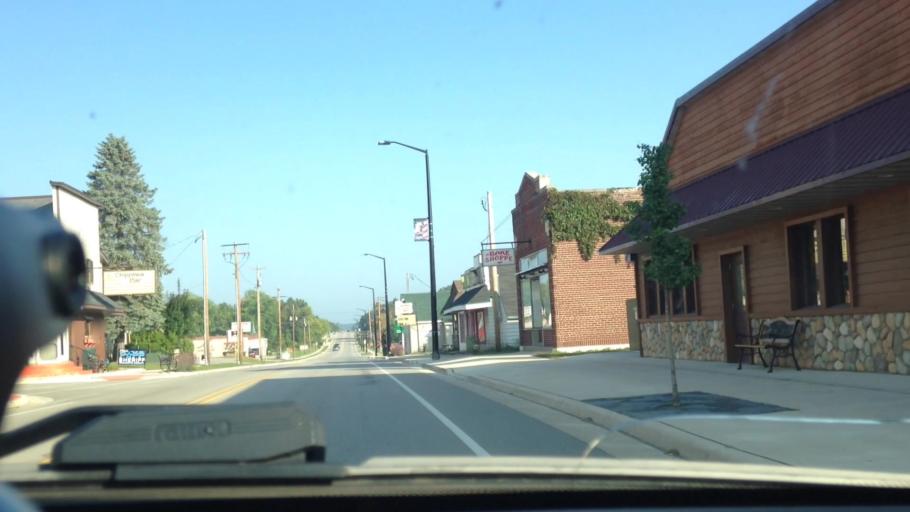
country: US
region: Wisconsin
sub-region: Marinette County
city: Peshtigo
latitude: 45.3763
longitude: -87.9528
